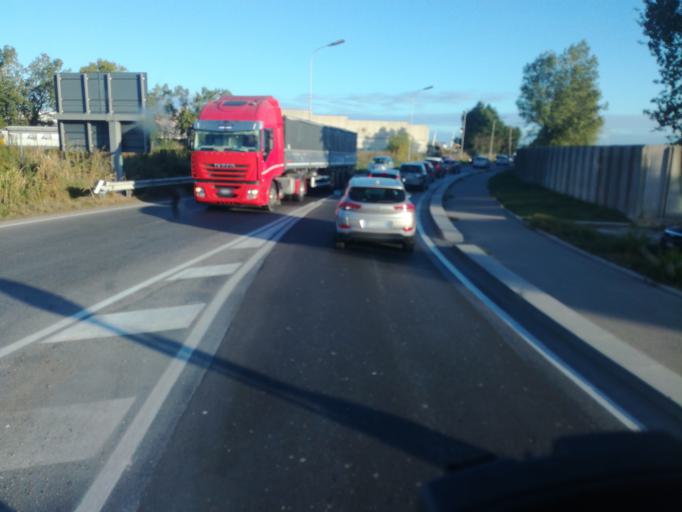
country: IT
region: Emilia-Romagna
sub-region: Provincia di Ravenna
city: Ravenna
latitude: 44.4257
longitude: 12.2273
